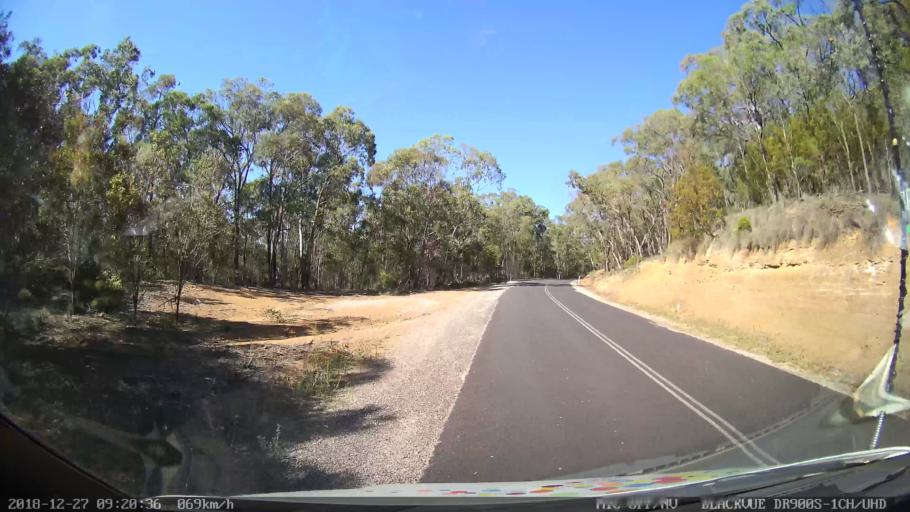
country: AU
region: New South Wales
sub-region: Lithgow
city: Portland
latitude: -33.1209
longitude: 150.0211
